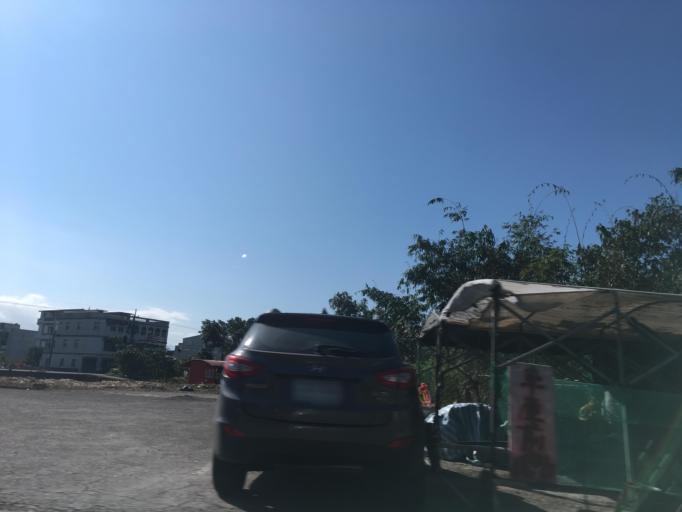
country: TW
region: Taiwan
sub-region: Yilan
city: Yilan
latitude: 24.7484
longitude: 121.7263
